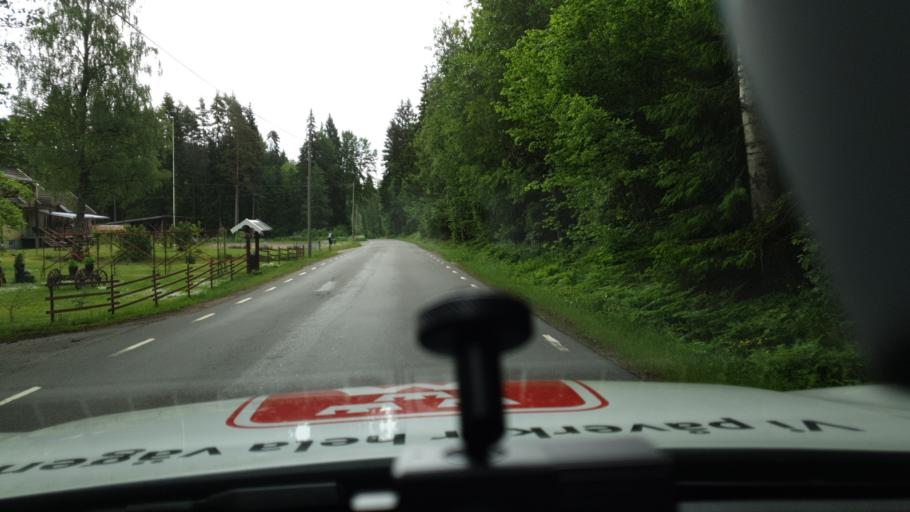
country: SE
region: Vaestra Goetaland
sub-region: Karlsborgs Kommun
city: Molltorp
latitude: 58.6683
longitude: 14.3735
